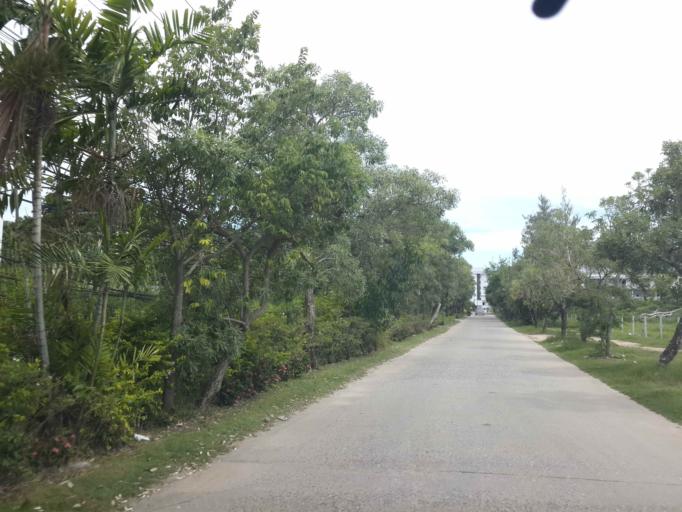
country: TH
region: Prachuap Khiri Khan
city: Hua Hin
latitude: 12.5343
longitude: 99.9675
